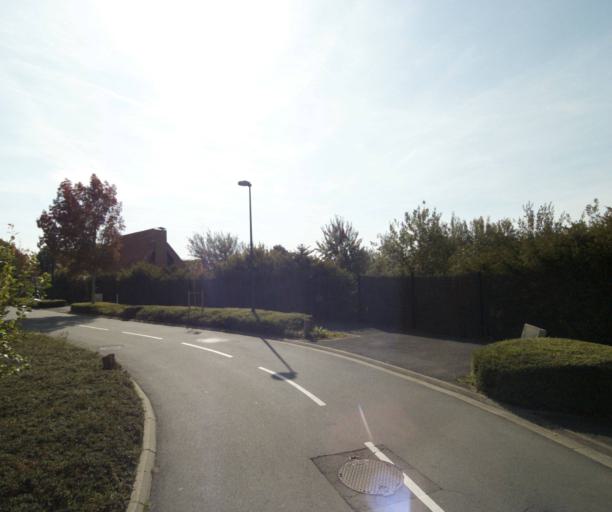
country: FR
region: Nord-Pas-de-Calais
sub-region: Departement du Nord
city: Capinghem
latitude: 50.6466
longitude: 2.9585
